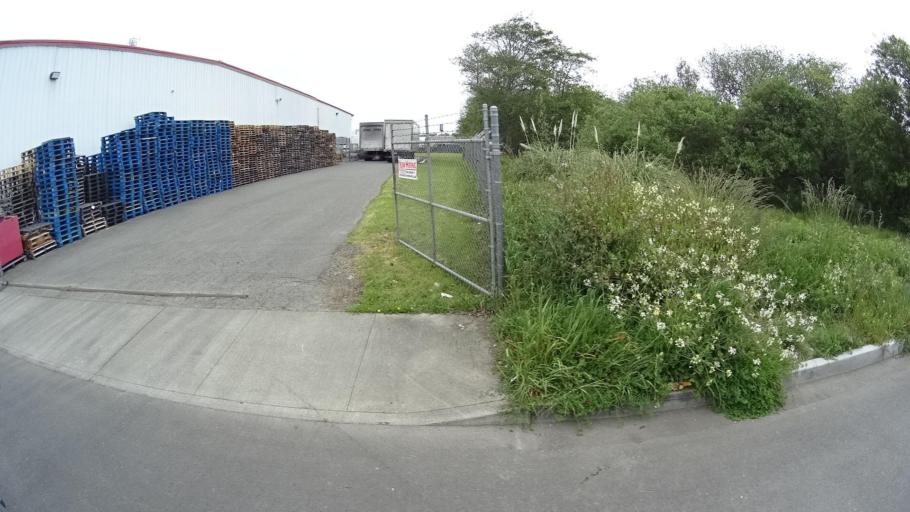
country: US
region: California
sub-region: Humboldt County
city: Bayview
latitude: 40.7898
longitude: -124.1840
